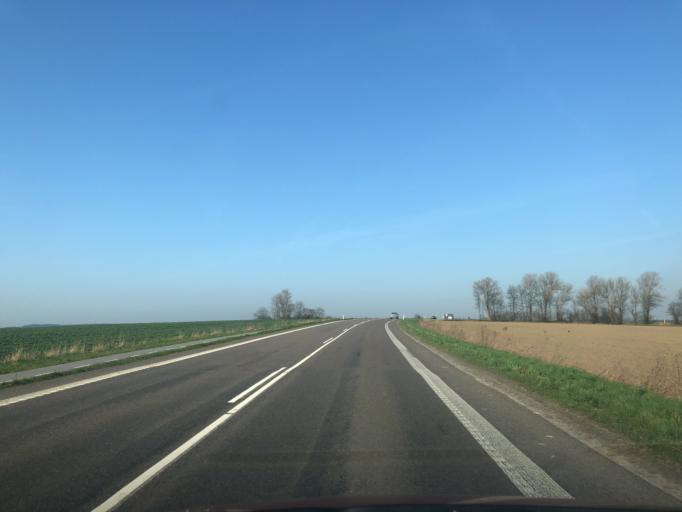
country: DK
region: Zealand
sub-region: Faxe Kommune
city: Fakse
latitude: 55.2547
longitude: 12.0895
